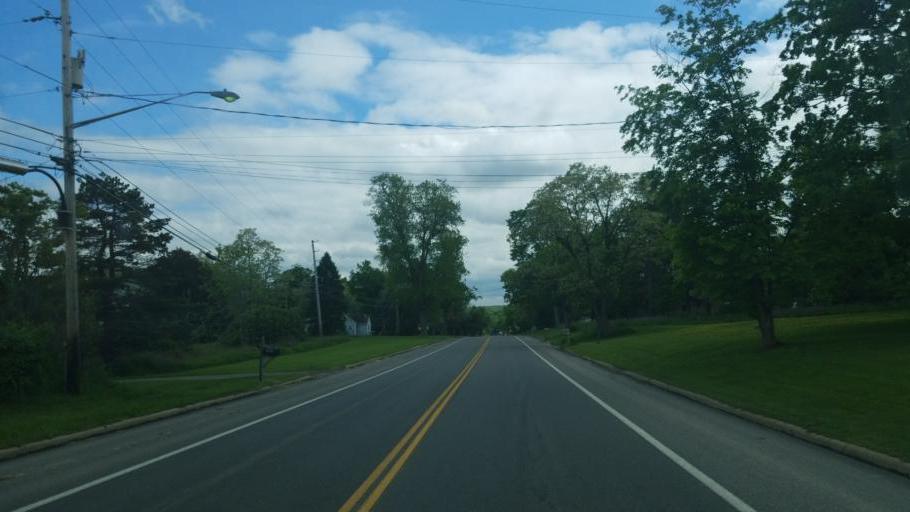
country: US
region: Ohio
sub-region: Geauga County
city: Middlefield
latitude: 41.3771
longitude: -81.0641
